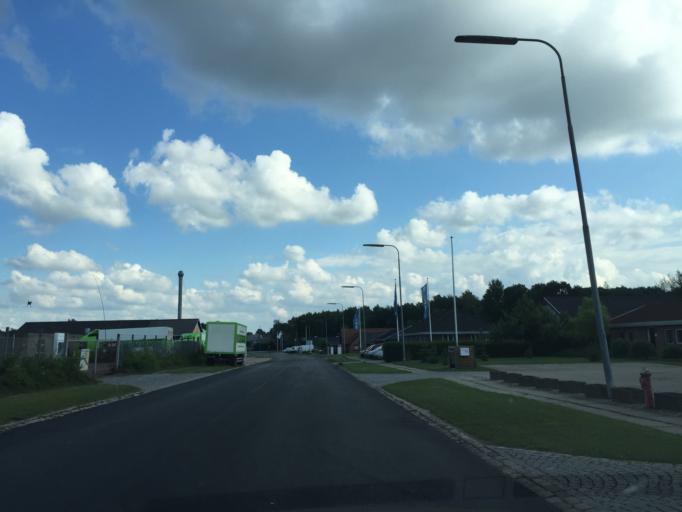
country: DK
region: South Denmark
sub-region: Odense Kommune
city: Neder Holluf
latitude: 55.3852
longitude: 10.4362
